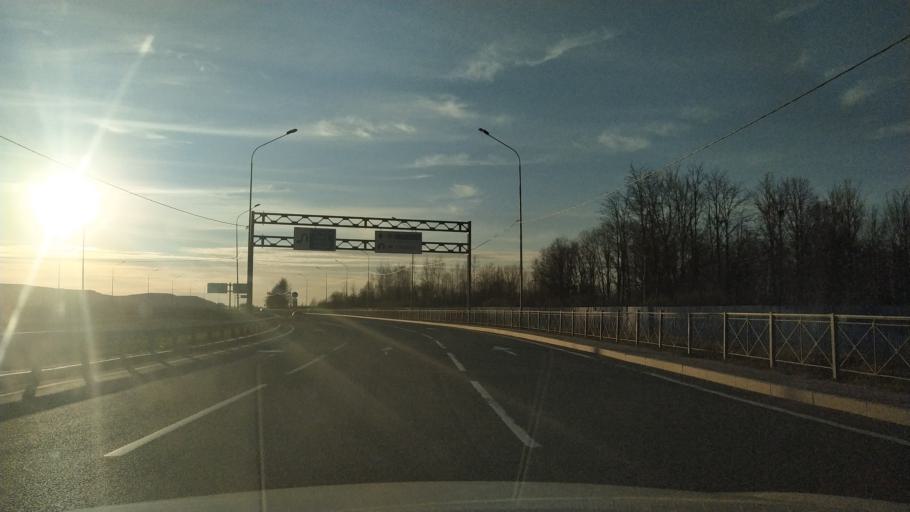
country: RU
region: St.-Petersburg
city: Aleksandrovskaya
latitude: 59.7473
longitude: 30.3026
